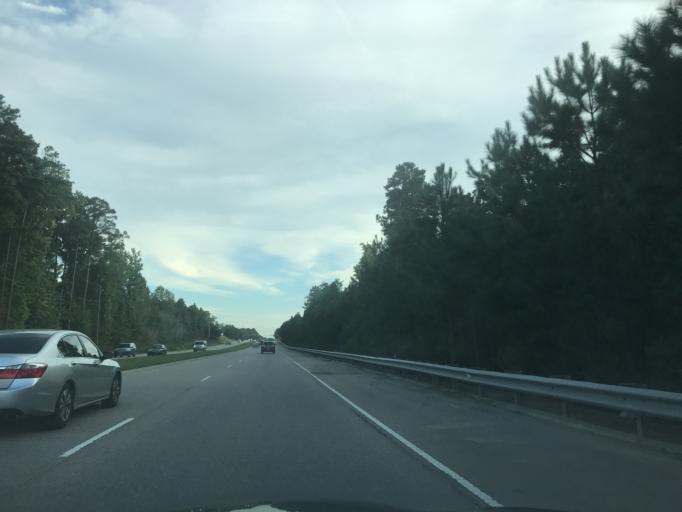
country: US
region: North Carolina
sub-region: Wake County
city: Green Level
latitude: 35.8087
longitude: -78.8721
